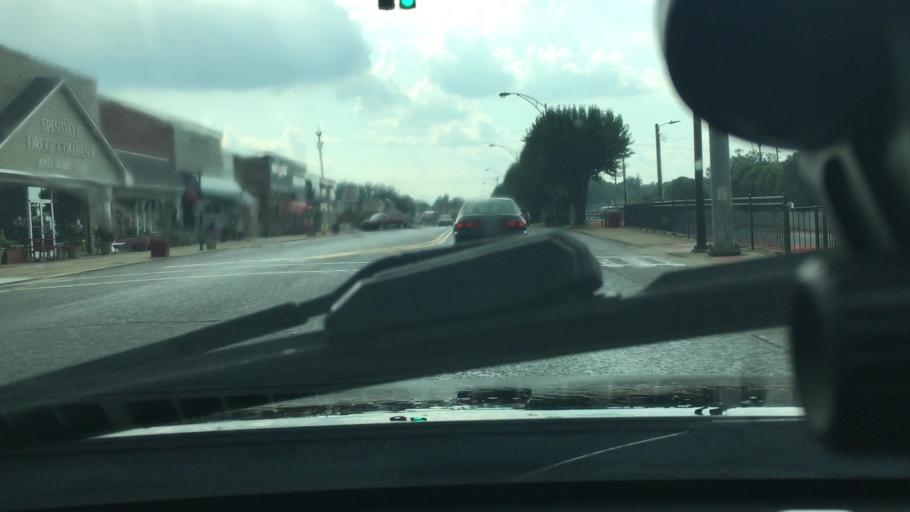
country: US
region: North Carolina
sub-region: Rutherford County
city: Spindale
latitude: 35.3573
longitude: -81.9305
